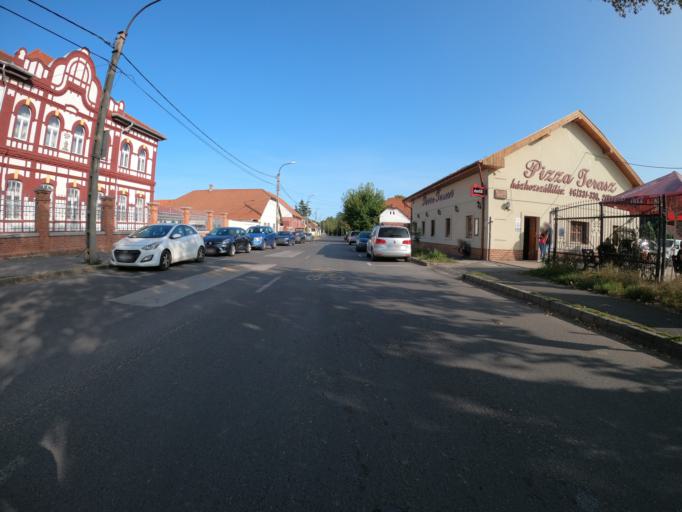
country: HU
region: Borsod-Abauj-Zemplen
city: Sajobabony
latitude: 48.1003
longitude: 20.6895
